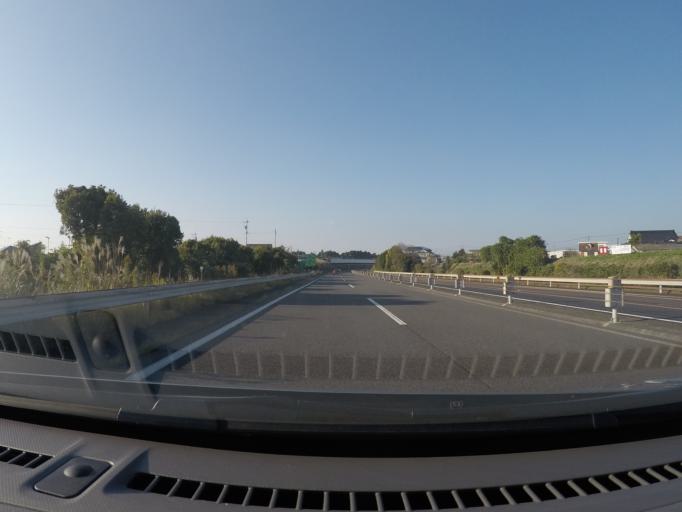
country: JP
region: Kagoshima
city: Kajiki
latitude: 31.8023
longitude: 130.7113
